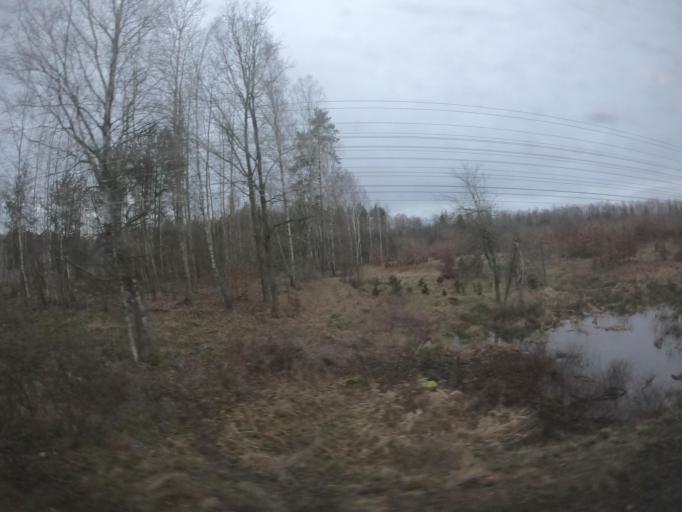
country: PL
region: West Pomeranian Voivodeship
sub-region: Powiat szczecinecki
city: Borne Sulinowo
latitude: 53.6479
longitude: 16.5286
